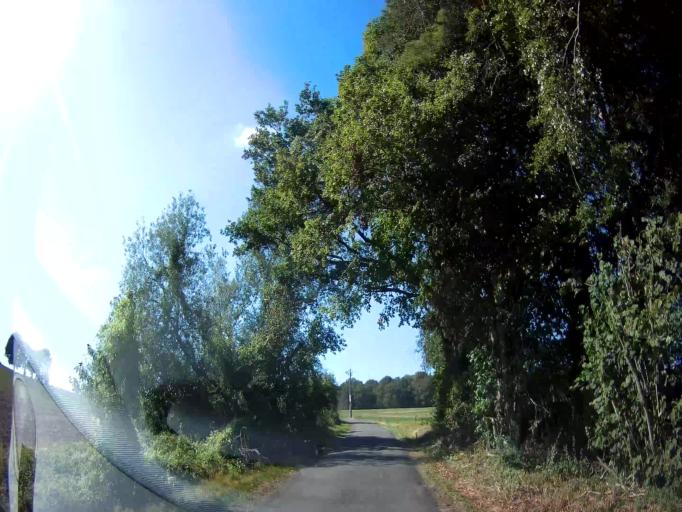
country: BE
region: Wallonia
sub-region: Province de Namur
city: Houyet
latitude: 50.2318
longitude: 4.9812
